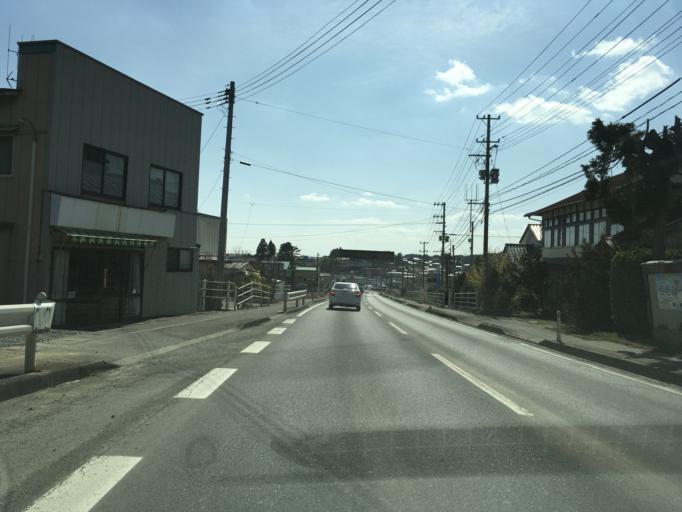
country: JP
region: Iwate
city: Ofunato
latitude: 38.8611
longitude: 141.5803
